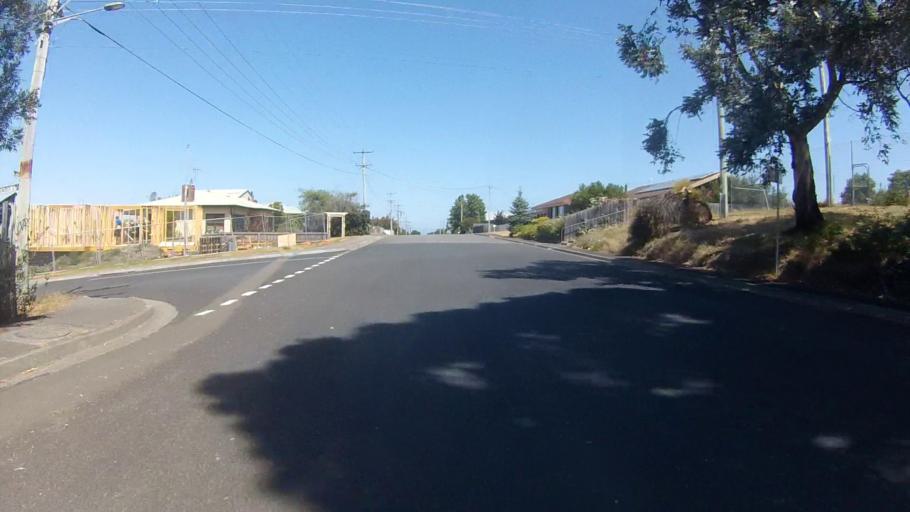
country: AU
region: Tasmania
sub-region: Sorell
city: Sorell
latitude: -42.7994
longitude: 147.5338
